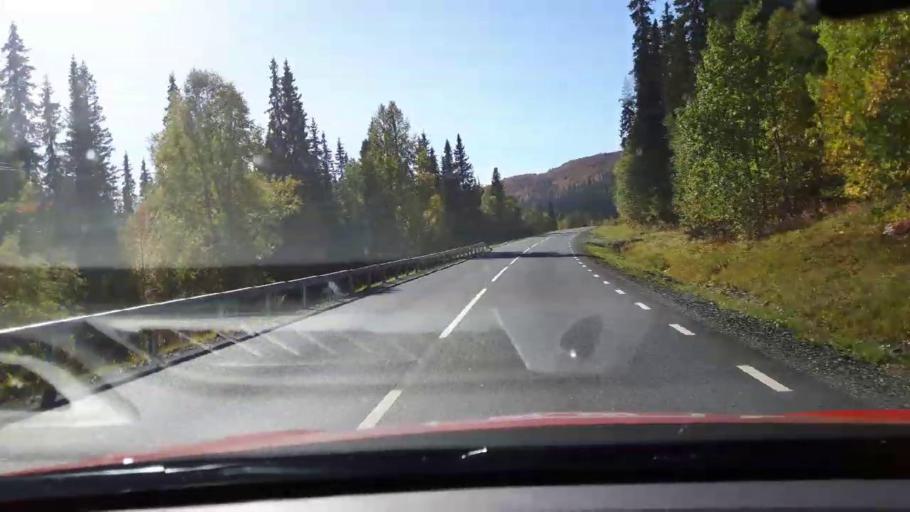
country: NO
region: Nord-Trondelag
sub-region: Royrvik
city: Royrvik
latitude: 64.8725
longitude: 14.2072
